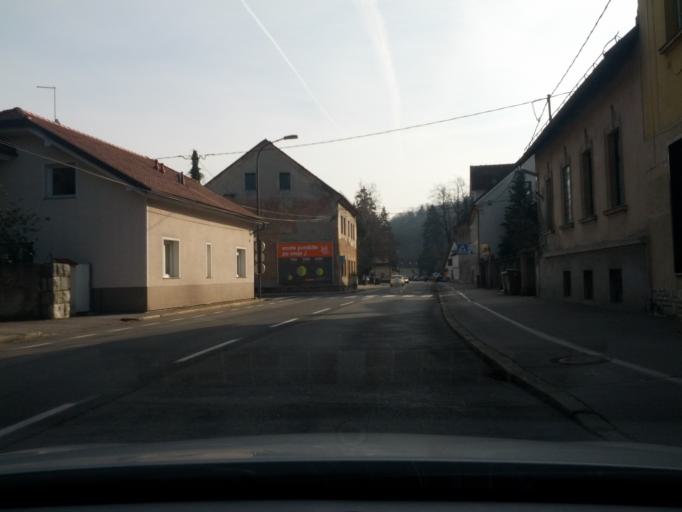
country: SI
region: Ljubljana
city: Ljubljana
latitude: 46.0684
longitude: 14.4846
